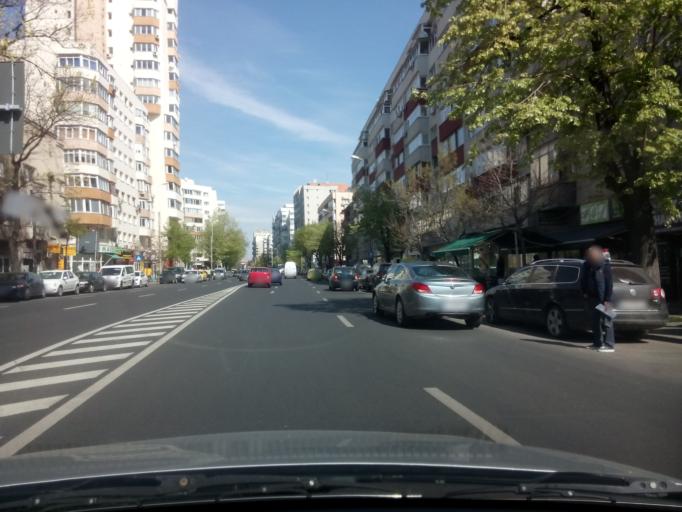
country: RO
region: Bucuresti
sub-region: Municipiul Bucuresti
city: Bucharest
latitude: 44.4539
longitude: 26.0983
